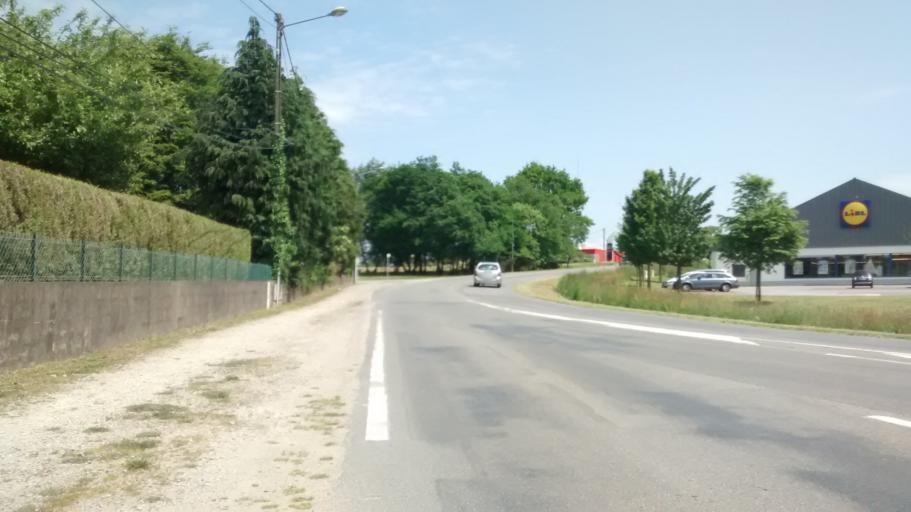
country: FR
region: Brittany
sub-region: Departement du Morbihan
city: Questembert
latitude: 47.6686
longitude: -2.4492
